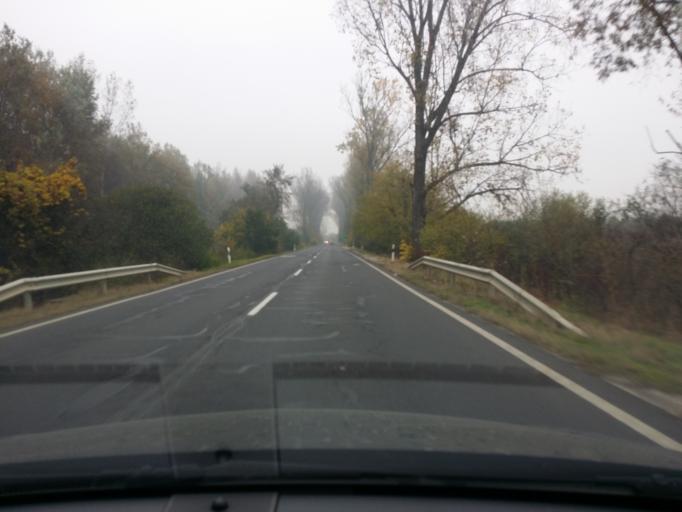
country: HU
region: Szabolcs-Szatmar-Bereg
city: Nyirpazony
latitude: 48.0166
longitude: 21.8381
